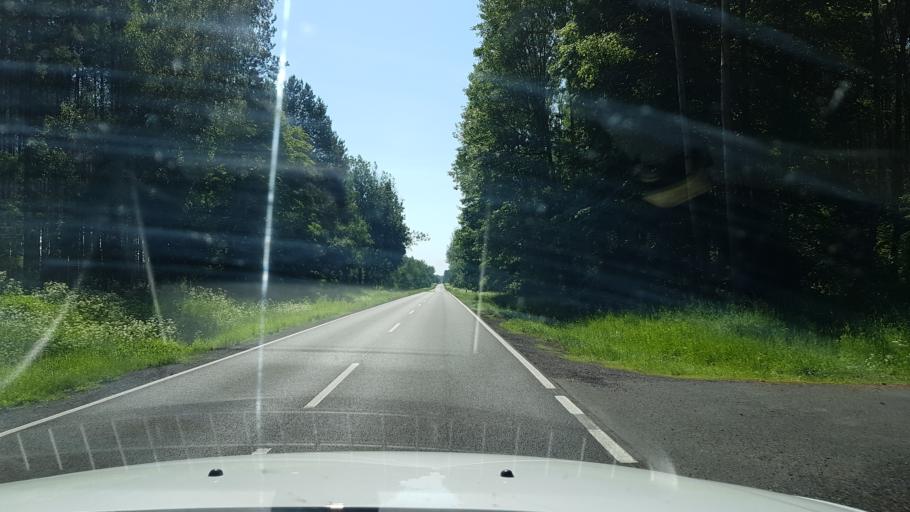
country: PL
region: West Pomeranian Voivodeship
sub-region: Powiat mysliborski
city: Boleszkowice
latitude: 52.7011
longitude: 14.6077
